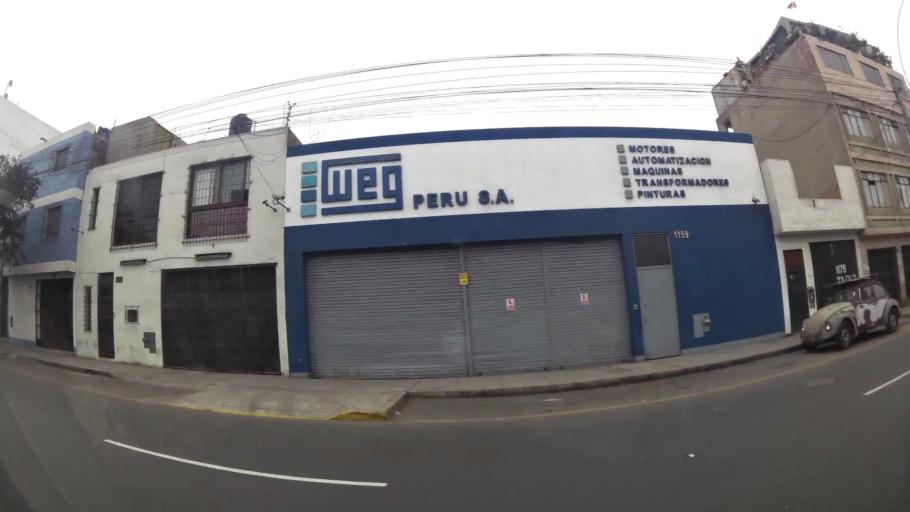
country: PE
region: Lima
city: Lima
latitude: -12.0720
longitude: -77.0297
